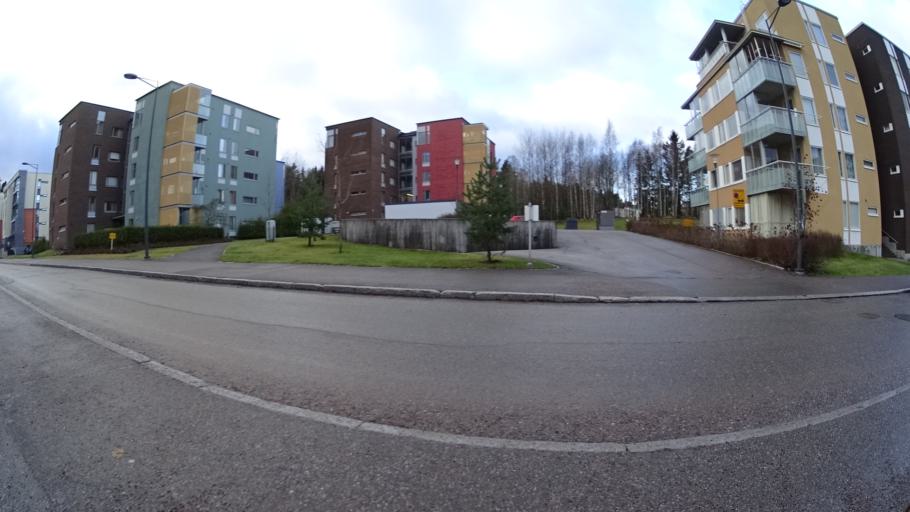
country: FI
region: Uusimaa
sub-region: Helsinki
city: Kauniainen
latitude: 60.1836
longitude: 24.7403
